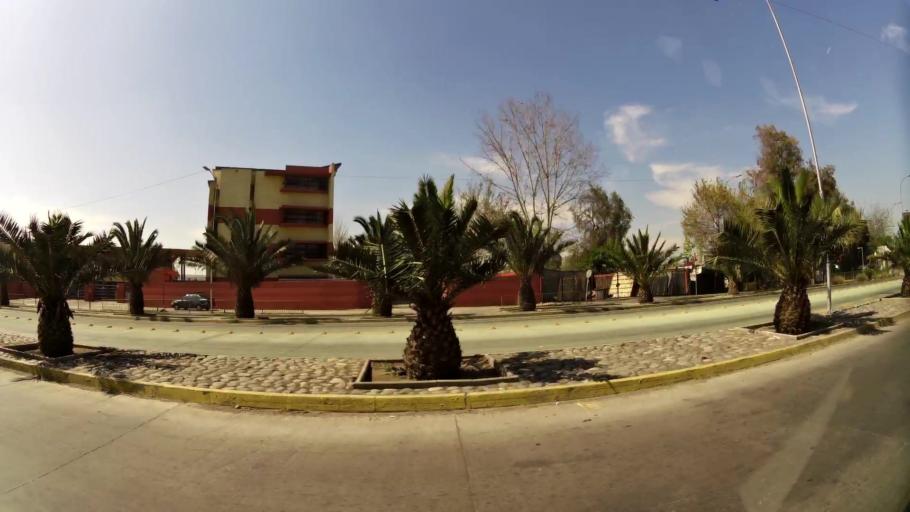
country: CL
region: Santiago Metropolitan
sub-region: Provincia de Santiago
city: Lo Prado
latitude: -33.4044
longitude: -70.7035
